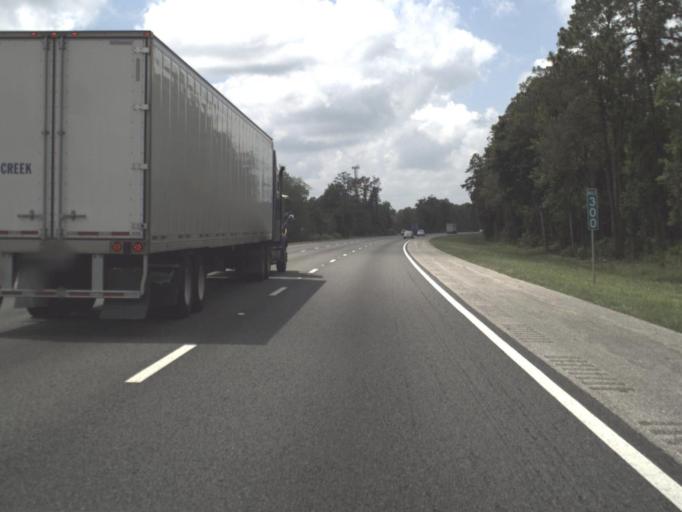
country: US
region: Florida
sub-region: Saint Johns County
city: Butler Beach
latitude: 29.6782
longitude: -81.3149
